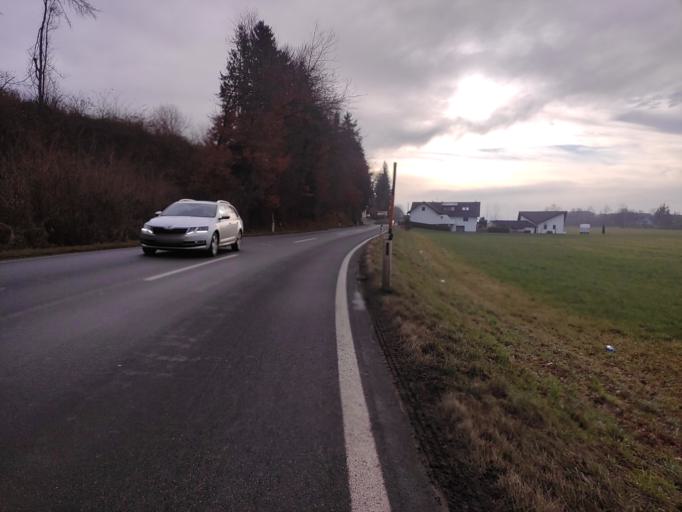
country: AT
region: Salzburg
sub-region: Politischer Bezirk Salzburg-Umgebung
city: Strasswalchen
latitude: 47.9950
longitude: 13.2397
